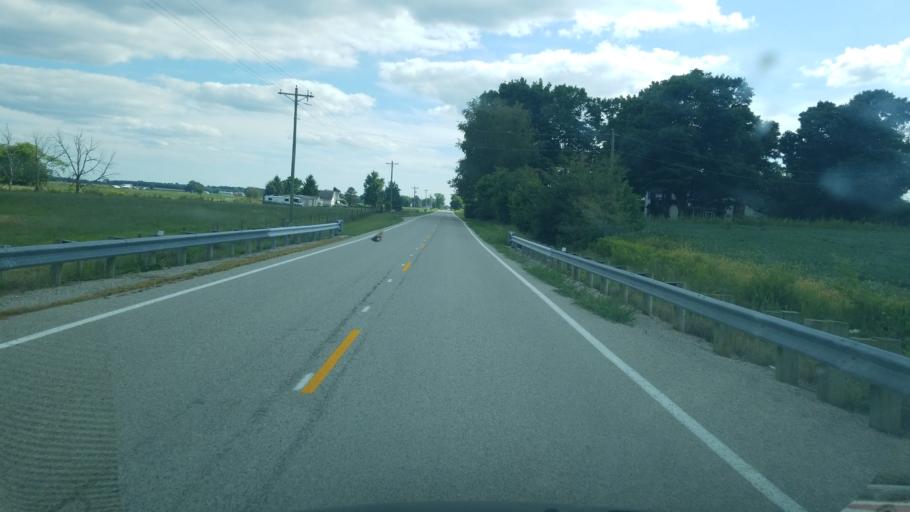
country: US
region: Ohio
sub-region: Logan County
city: De Graff
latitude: 40.2376
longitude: -83.9391
